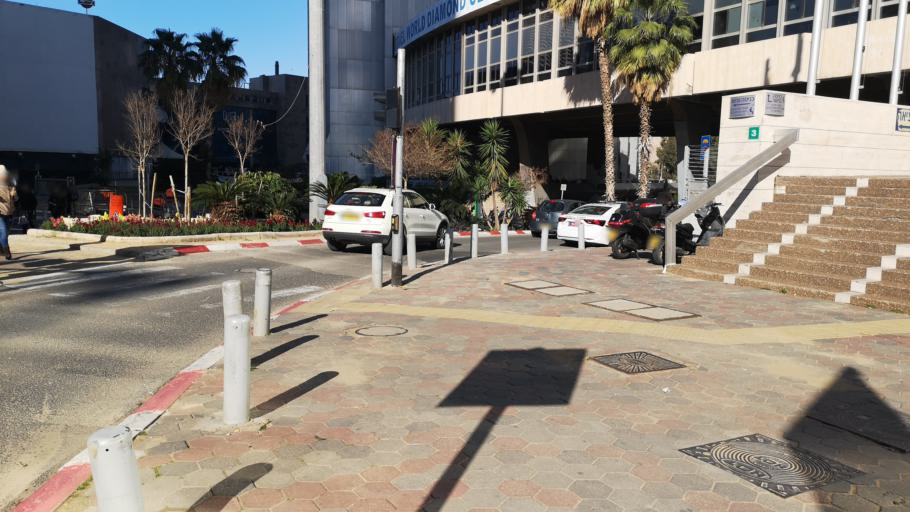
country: IL
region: Tel Aviv
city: Ramat Gan
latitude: 32.0827
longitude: 34.8009
